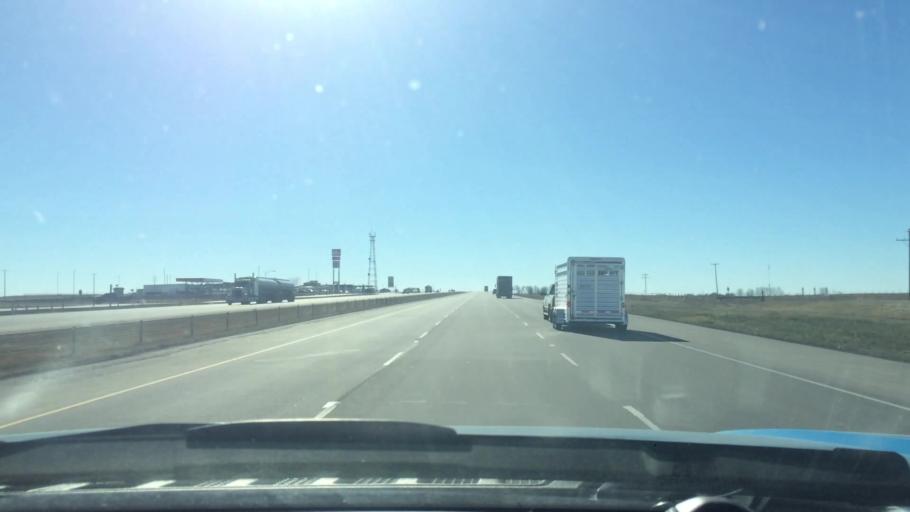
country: CA
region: Alberta
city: Crossfield
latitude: 51.4178
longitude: -114.0021
